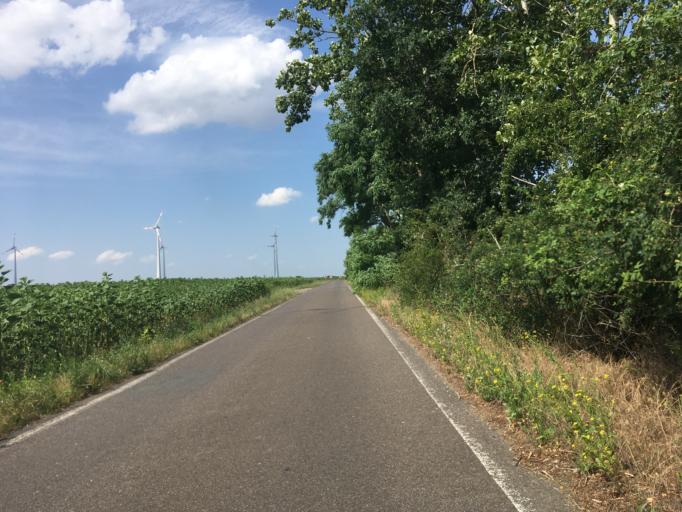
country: DE
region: Saxony-Anhalt
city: Quellendorf
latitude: 51.7830
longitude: 12.1466
